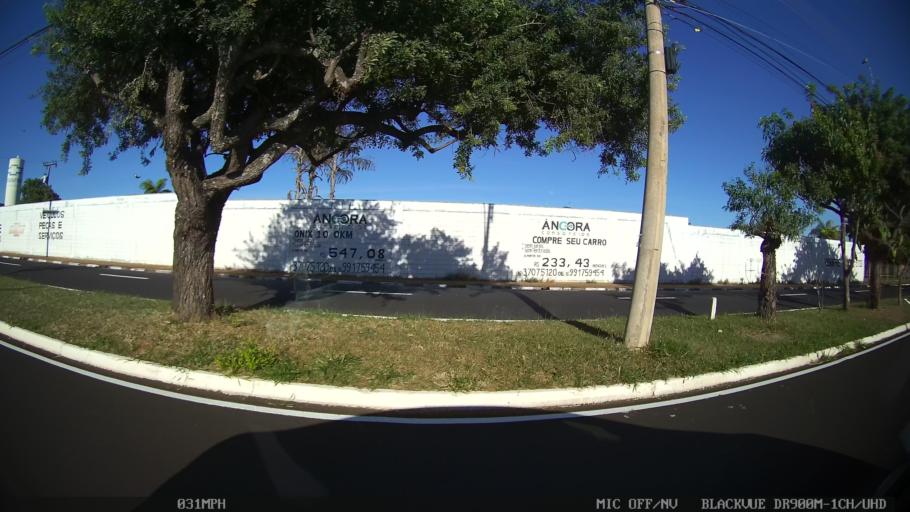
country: BR
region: Sao Paulo
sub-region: Franca
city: Franca
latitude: -20.5681
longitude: -47.3947
